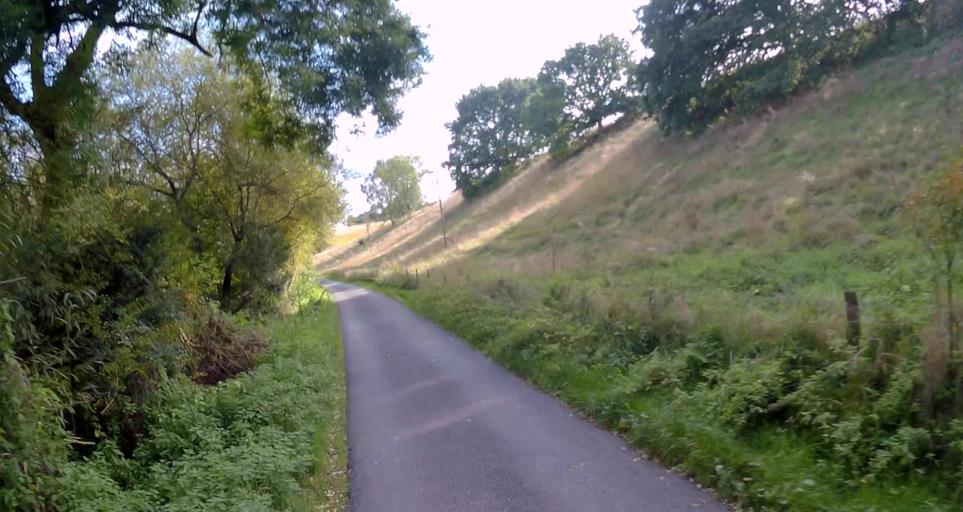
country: GB
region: England
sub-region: Hampshire
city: Kings Worthy
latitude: 51.0884
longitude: -1.2215
